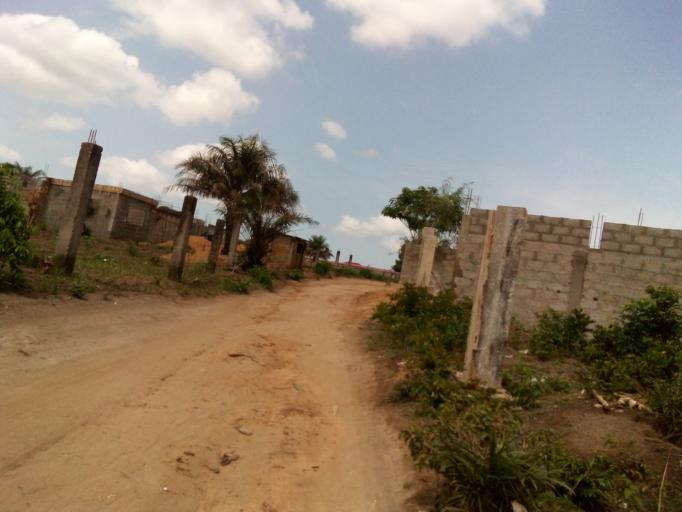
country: SL
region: Western Area
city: Waterloo
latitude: 8.3439
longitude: -13.0260
